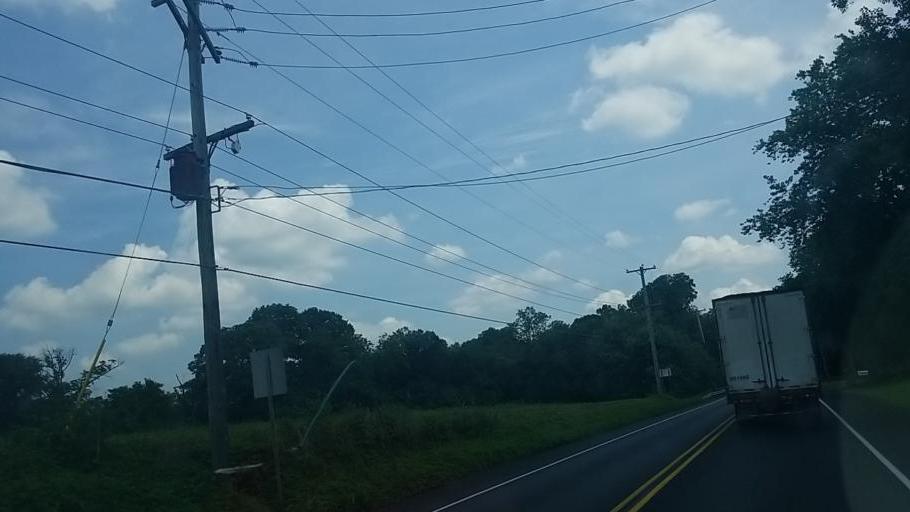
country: US
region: Pennsylvania
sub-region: Chester County
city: Toughkenamon
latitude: 39.8142
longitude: -75.7628
